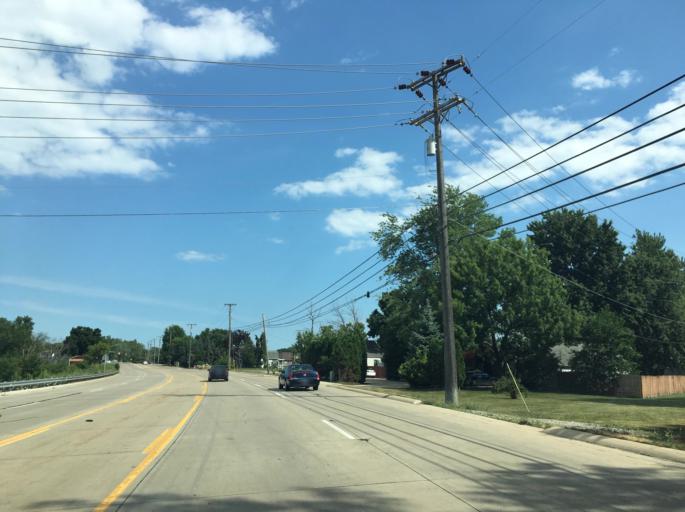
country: US
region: Michigan
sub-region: Macomb County
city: Clinton
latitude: 42.6071
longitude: -82.9214
